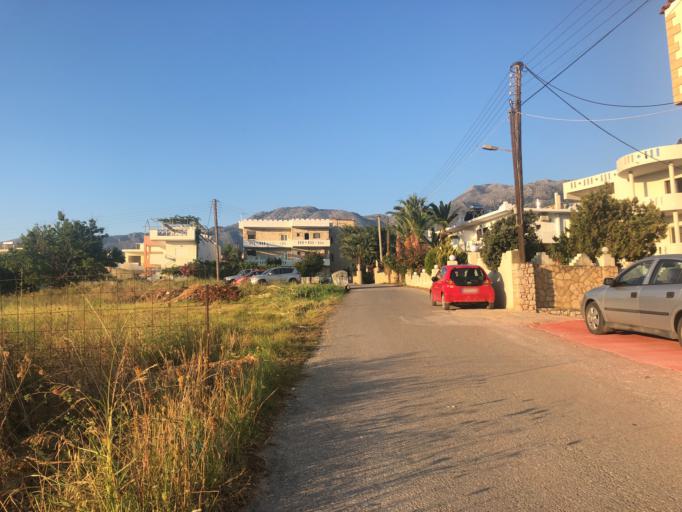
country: GR
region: Crete
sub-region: Nomos Chanias
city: Georgioupolis
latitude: 35.3463
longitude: 24.3013
